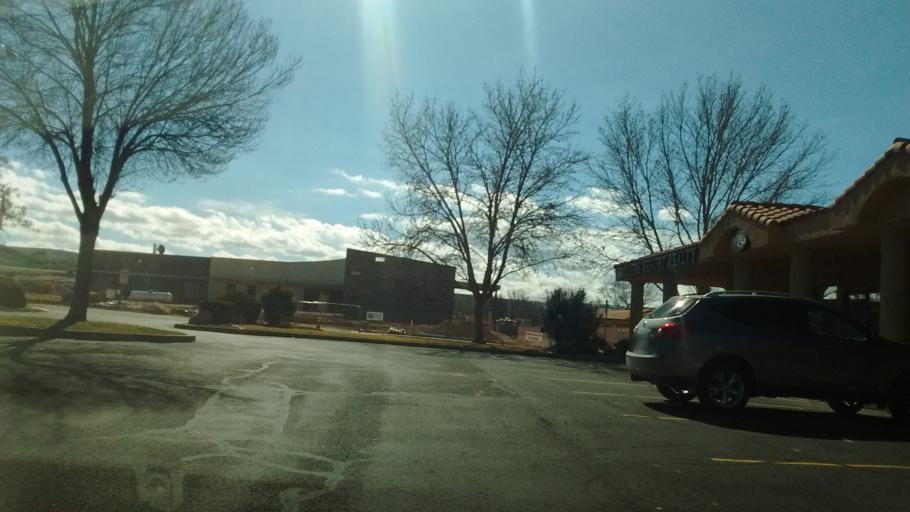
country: US
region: Utah
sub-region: Washington County
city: Saint George
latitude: 37.0608
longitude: -113.5874
